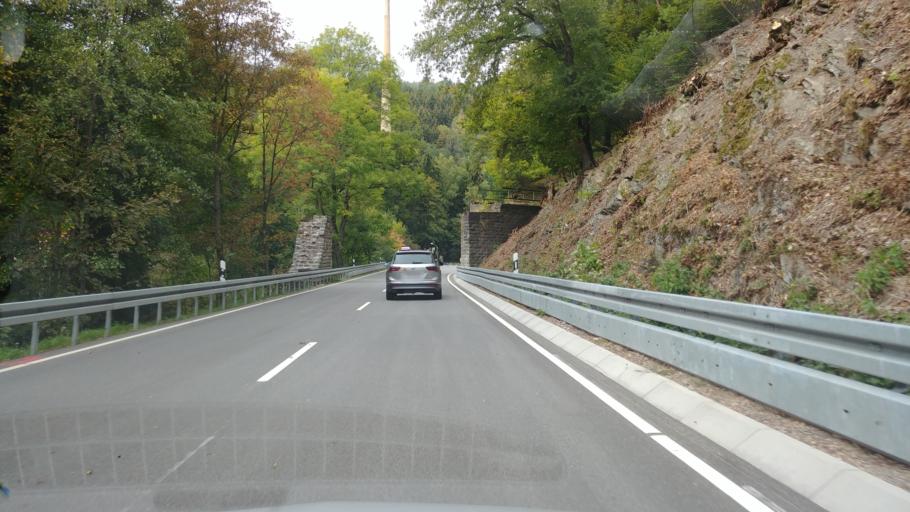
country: DE
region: Rheinland-Pfalz
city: Reckenroth
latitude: 50.2205
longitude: 8.0368
